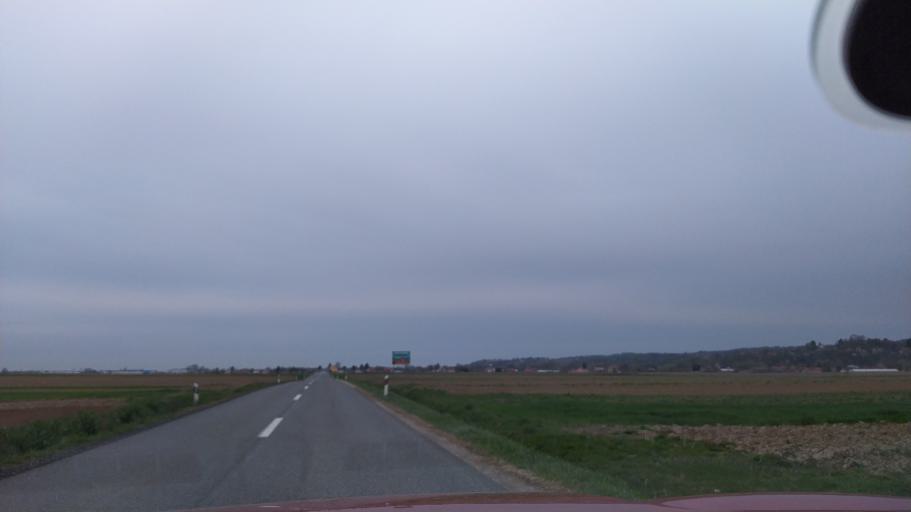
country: HR
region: Varazdinska
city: Ludbreg
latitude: 46.2504
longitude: 16.5678
